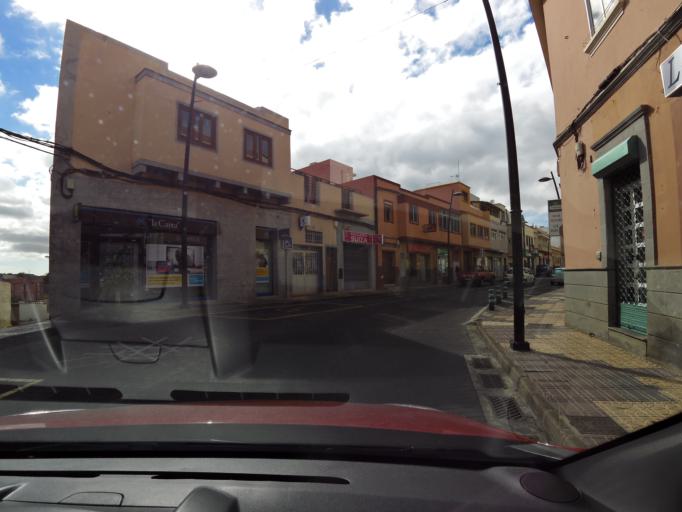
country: ES
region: Canary Islands
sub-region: Provincia de Las Palmas
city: Ingenio
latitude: 27.9198
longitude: -15.4371
